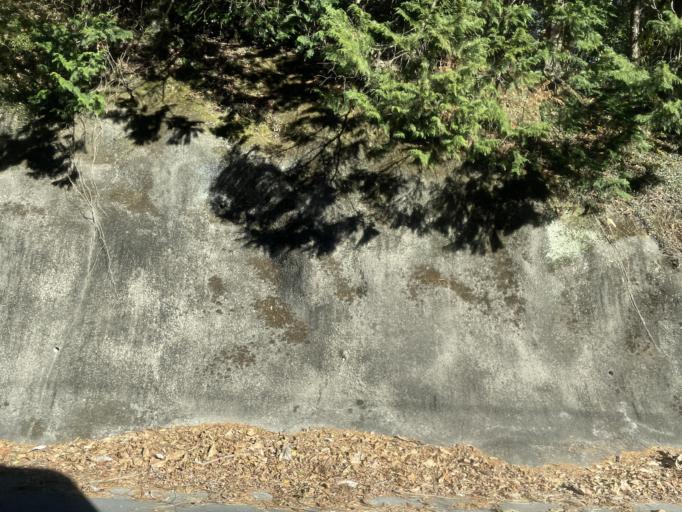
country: JP
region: Saitama
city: Yorii
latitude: 36.0614
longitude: 139.1875
